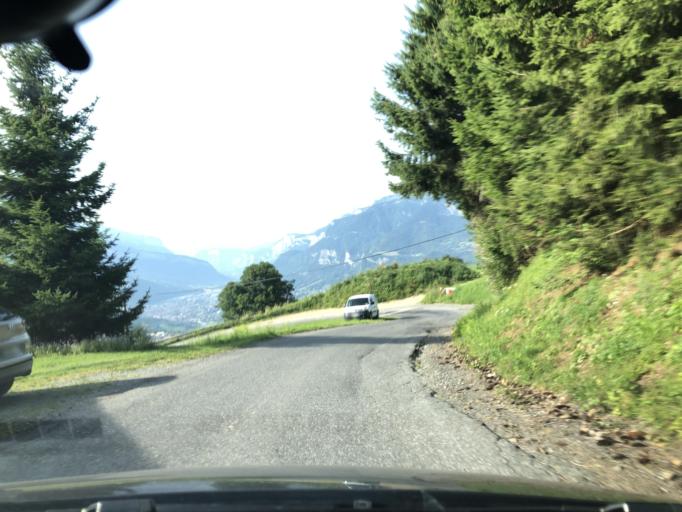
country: FR
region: Rhone-Alpes
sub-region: Departement de la Haute-Savoie
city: Combloux
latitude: 45.8846
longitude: 6.6545
